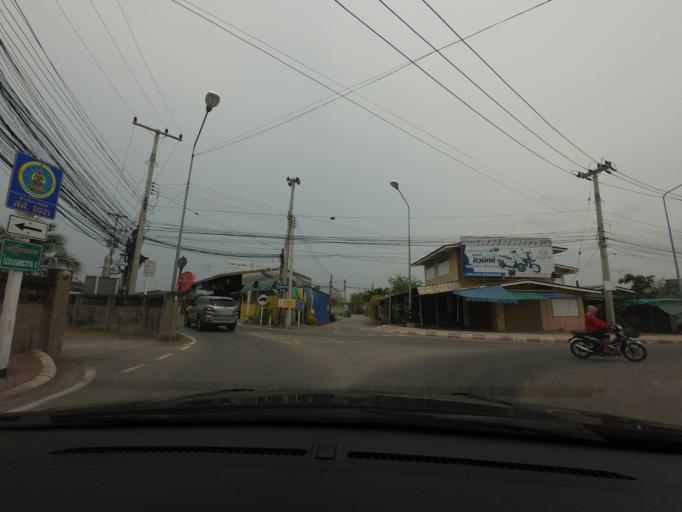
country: TH
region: Phetchaburi
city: Ban Laem
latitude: 13.2137
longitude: 99.9797
